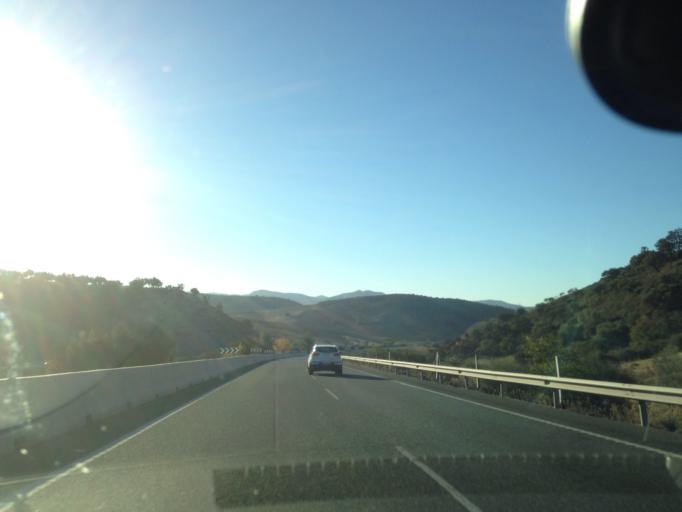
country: ES
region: Andalusia
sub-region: Provincia de Malaga
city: Casabermeja
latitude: 36.9469
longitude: -4.4418
